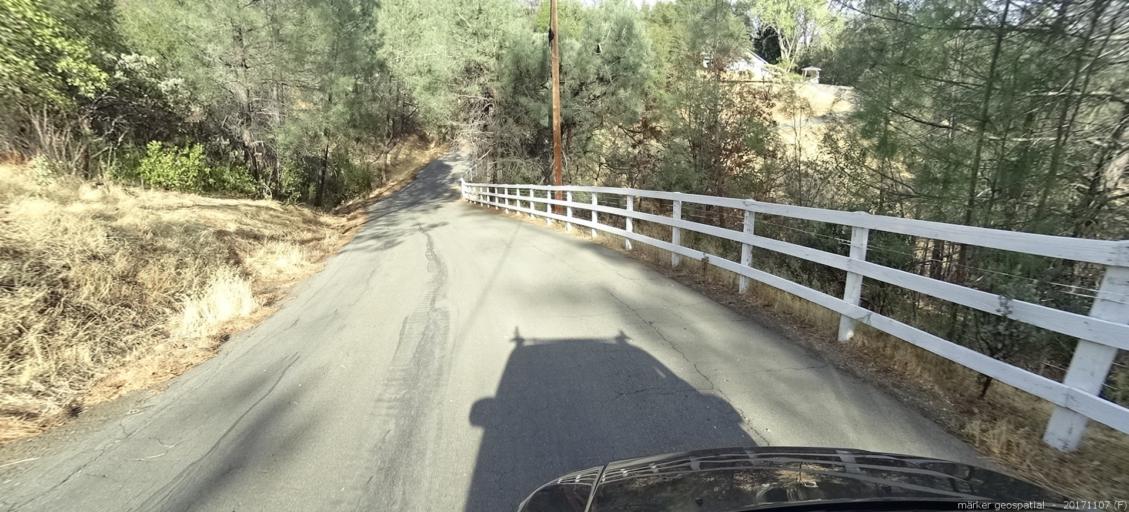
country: US
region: California
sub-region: Shasta County
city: Shasta
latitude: 40.5238
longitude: -122.4979
